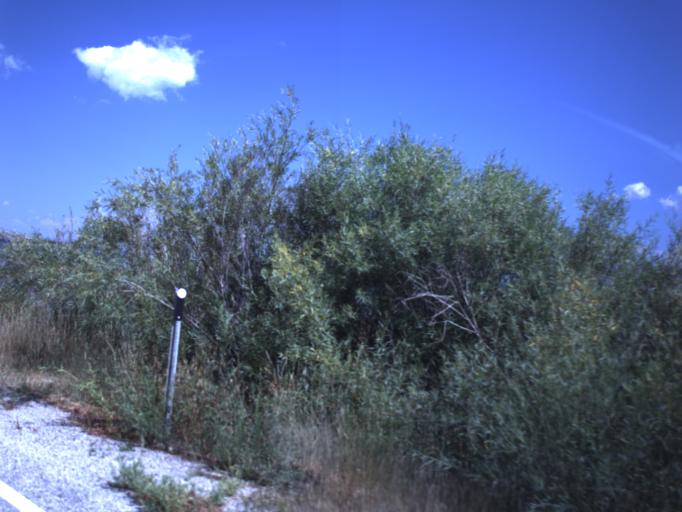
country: US
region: Idaho
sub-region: Bear Lake County
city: Paris
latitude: 41.9778
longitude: -111.4030
